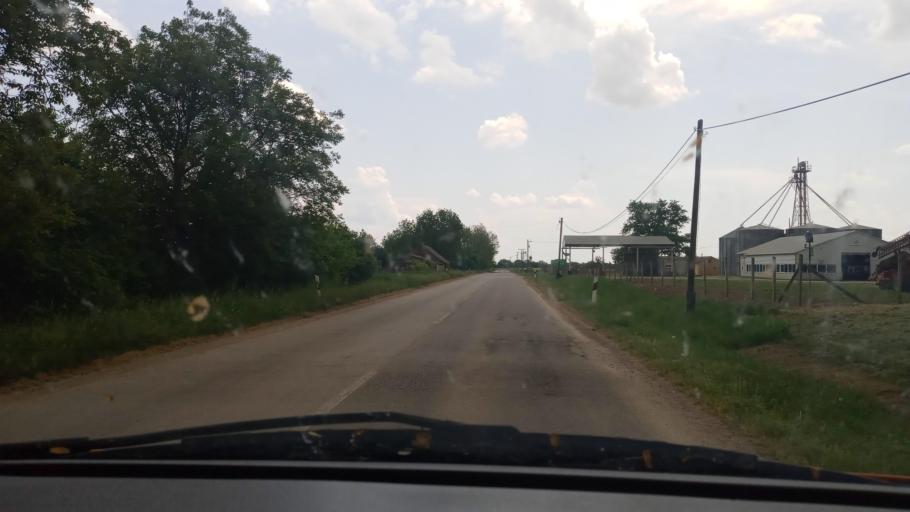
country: HU
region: Baranya
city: Beremend
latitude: 45.7733
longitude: 18.4460
